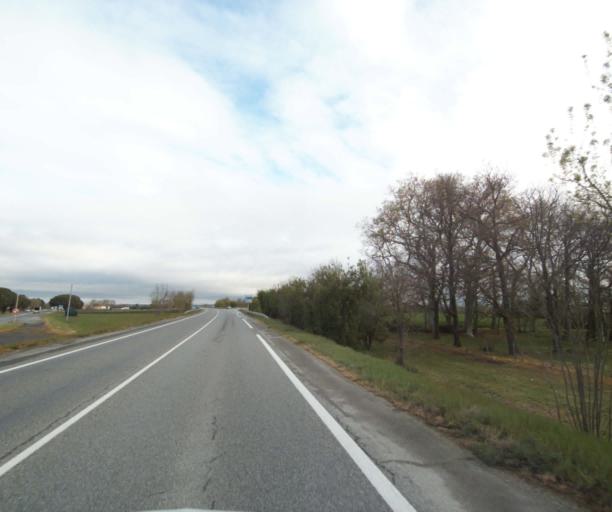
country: FR
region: Midi-Pyrenees
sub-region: Departement de l'Ariege
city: Saverdun
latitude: 43.2243
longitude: 1.6064
